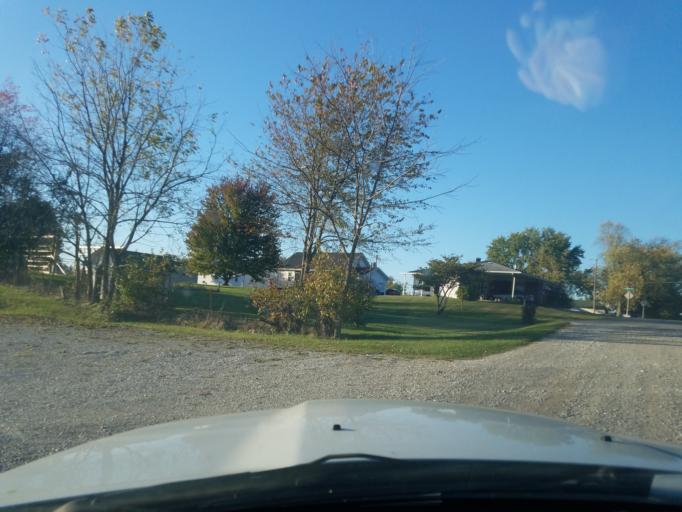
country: US
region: Indiana
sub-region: Washington County
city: Salem
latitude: 38.5949
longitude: -86.0954
